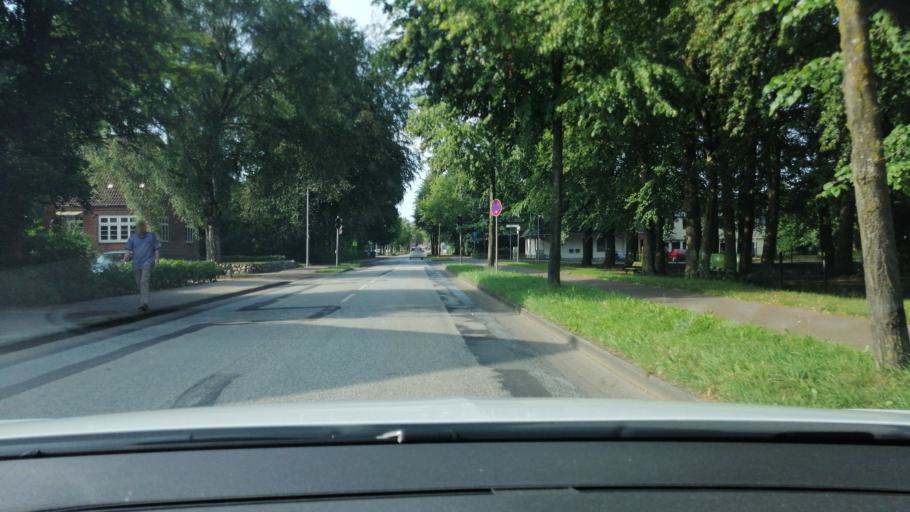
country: DE
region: Schleswig-Holstein
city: Leck
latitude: 54.7680
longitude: 8.9776
